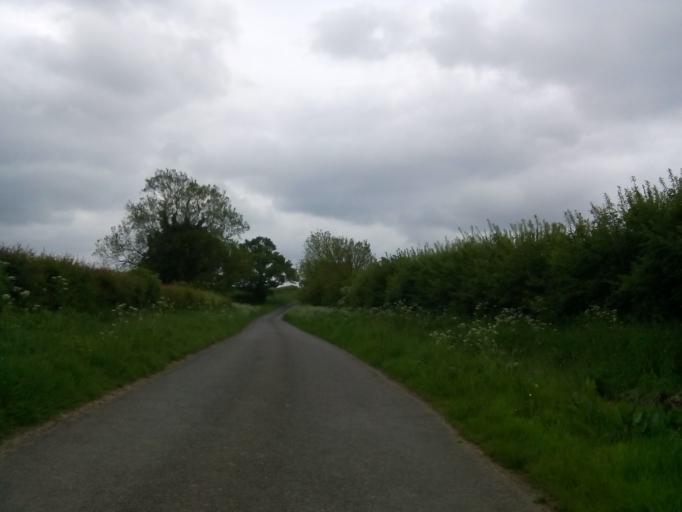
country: GB
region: England
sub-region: District of Rutland
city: Seaton
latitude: 52.5305
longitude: -0.6173
